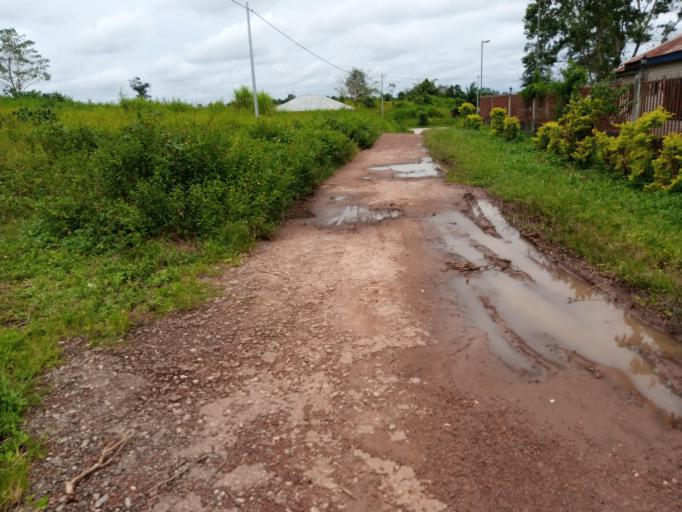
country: SL
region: Southern Province
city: Largo
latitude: 8.1994
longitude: -12.0659
